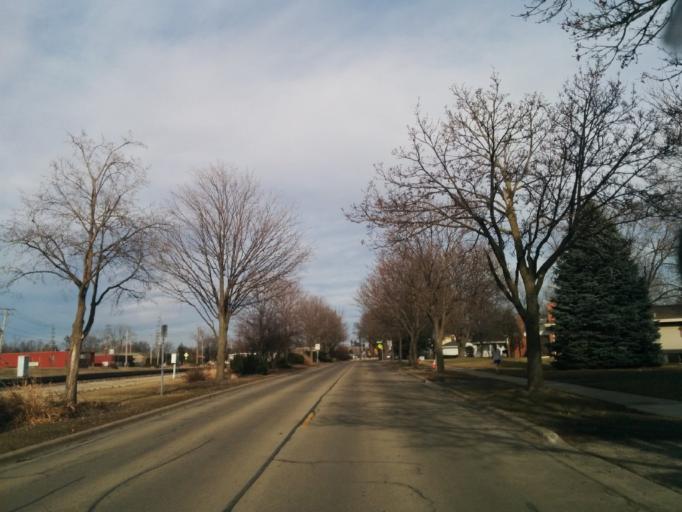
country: US
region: Illinois
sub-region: DuPage County
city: Lombard
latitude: 41.8885
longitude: -88.0112
